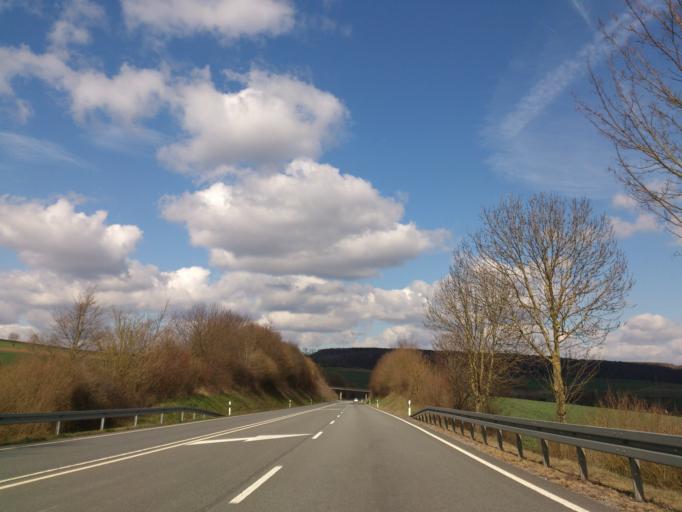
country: DE
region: North Rhine-Westphalia
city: Brakel
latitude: 51.7060
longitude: 9.2303
